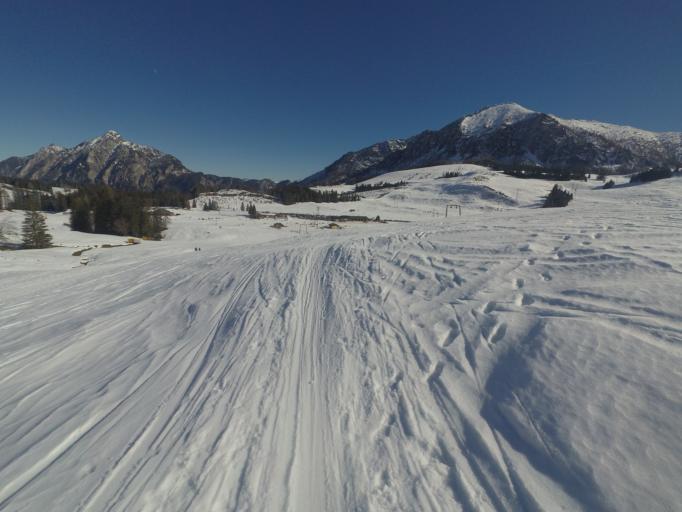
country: AT
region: Salzburg
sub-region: Politischer Bezirk Salzburg-Umgebung
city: Strobl
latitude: 47.6497
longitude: 13.4253
